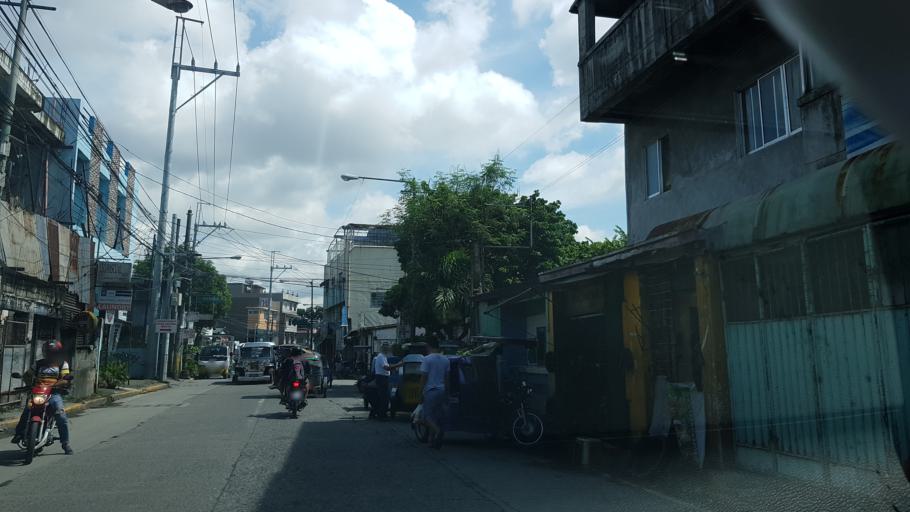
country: PH
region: Calabarzon
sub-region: Province of Rizal
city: Pateros
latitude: 14.5426
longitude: 121.0597
